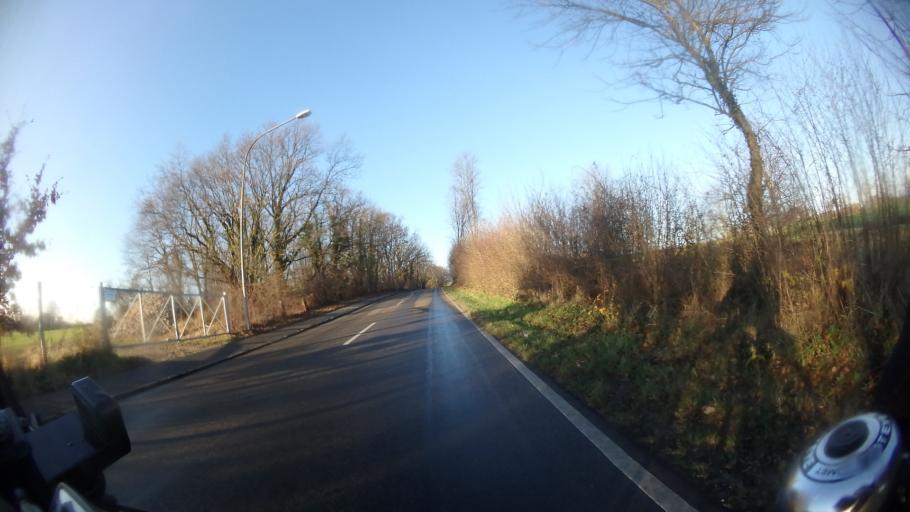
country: DE
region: Schleswig-Holstein
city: Travemuende
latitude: 53.9793
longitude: 10.8649
